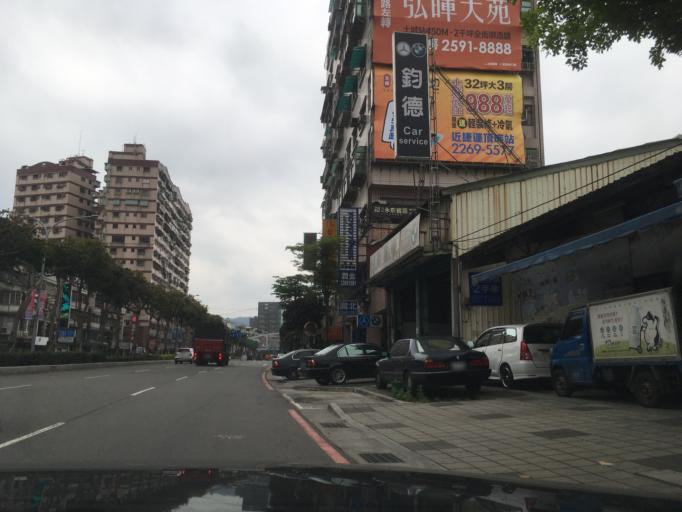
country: TW
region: Taipei
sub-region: Taipei
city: Banqiao
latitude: 24.9780
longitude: 121.4392
